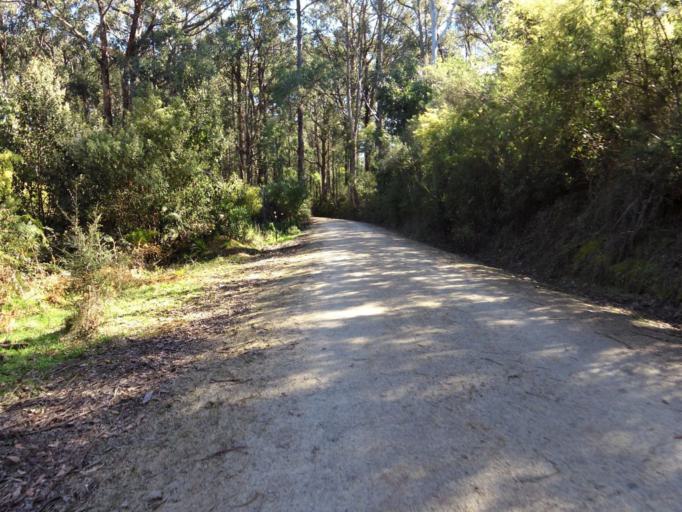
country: AU
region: Victoria
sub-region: Latrobe
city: Moe
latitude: -38.3904
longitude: 146.1826
